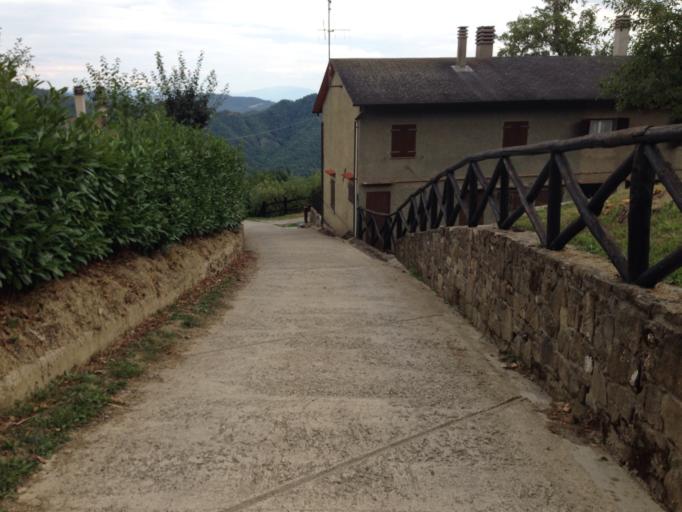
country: IT
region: Tuscany
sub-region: Provincia di Prato
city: Cantagallo
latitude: 44.0695
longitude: 11.0914
